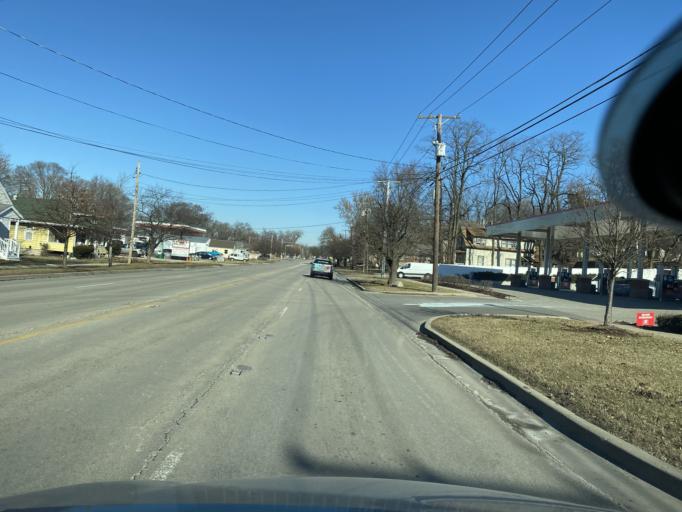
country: US
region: Illinois
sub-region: Will County
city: Lockport
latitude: 41.5946
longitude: -88.0549
